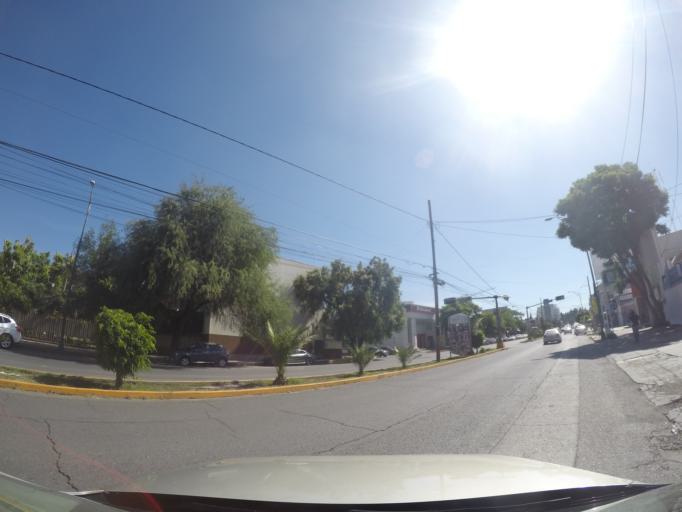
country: MX
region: San Luis Potosi
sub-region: San Luis Potosi
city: San Luis Potosi
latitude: 22.1487
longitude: -101.0123
